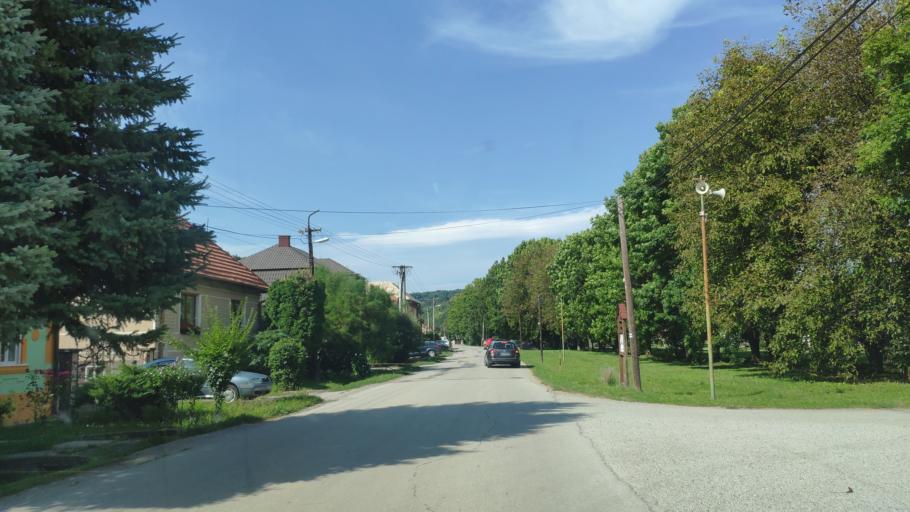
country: HU
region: Borsod-Abauj-Zemplen
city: Putnok
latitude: 48.4466
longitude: 20.3159
